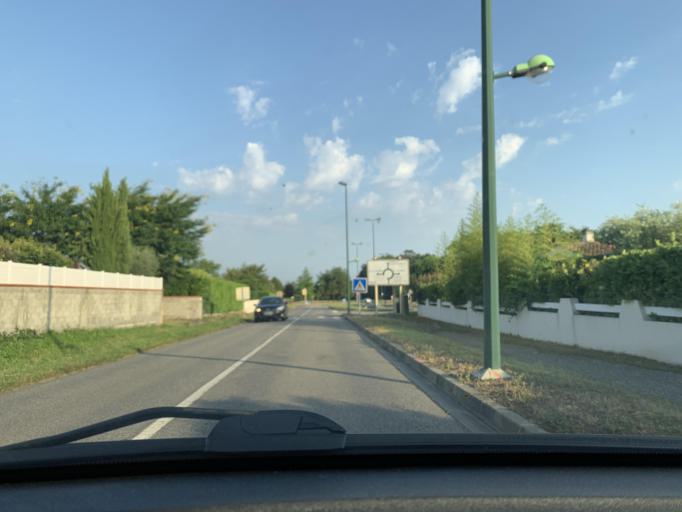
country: FR
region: Midi-Pyrenees
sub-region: Departement de la Haute-Garonne
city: Escalquens
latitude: 43.5301
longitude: 1.5534
